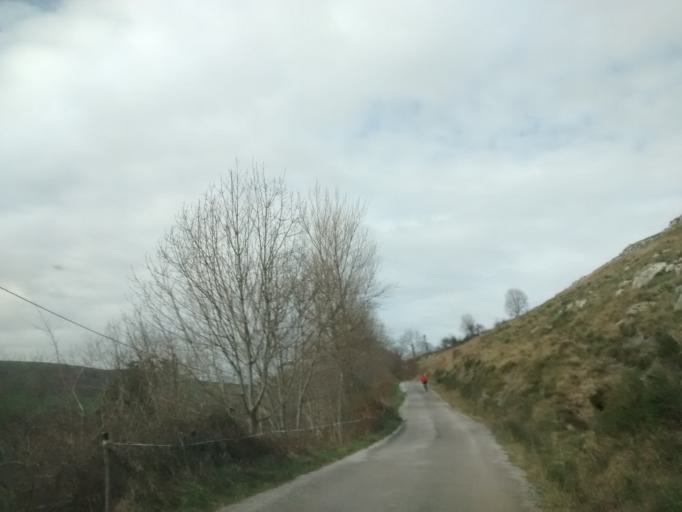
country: ES
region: Cantabria
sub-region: Provincia de Cantabria
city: Lierganes
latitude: 43.3240
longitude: -3.7302
